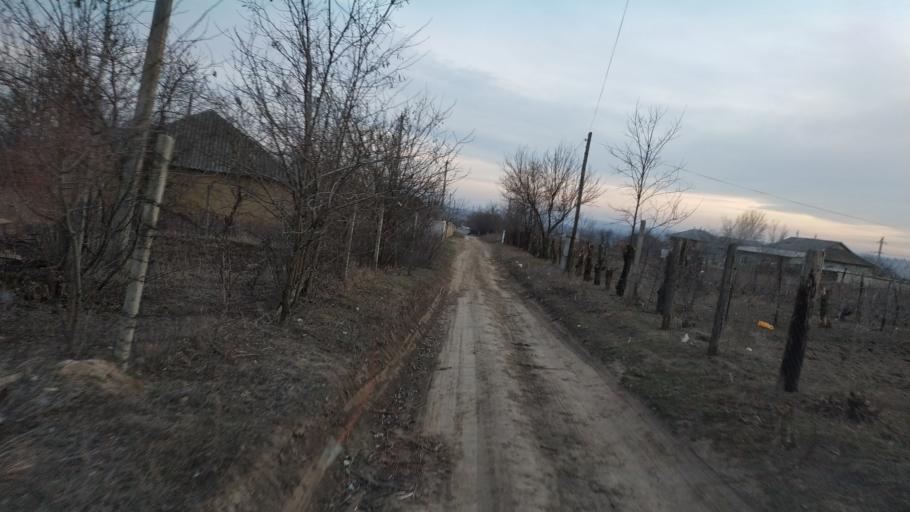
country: MD
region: Hincesti
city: Dancu
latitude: 46.7494
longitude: 28.2106
